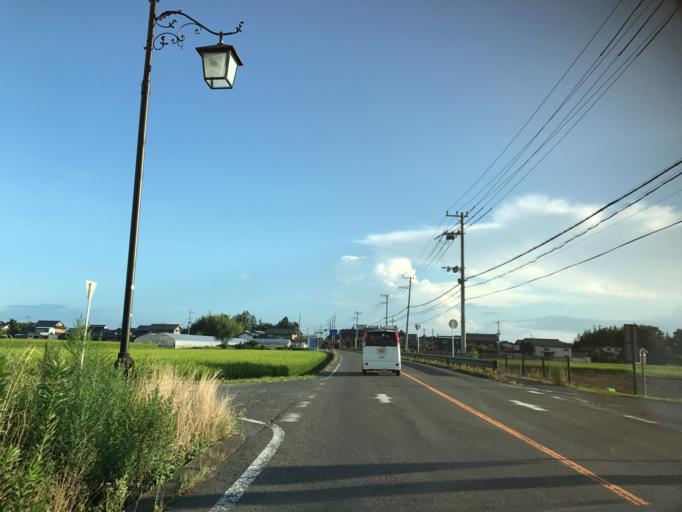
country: JP
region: Shiga Prefecture
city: Youkaichi
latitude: 35.1277
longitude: 136.2591
